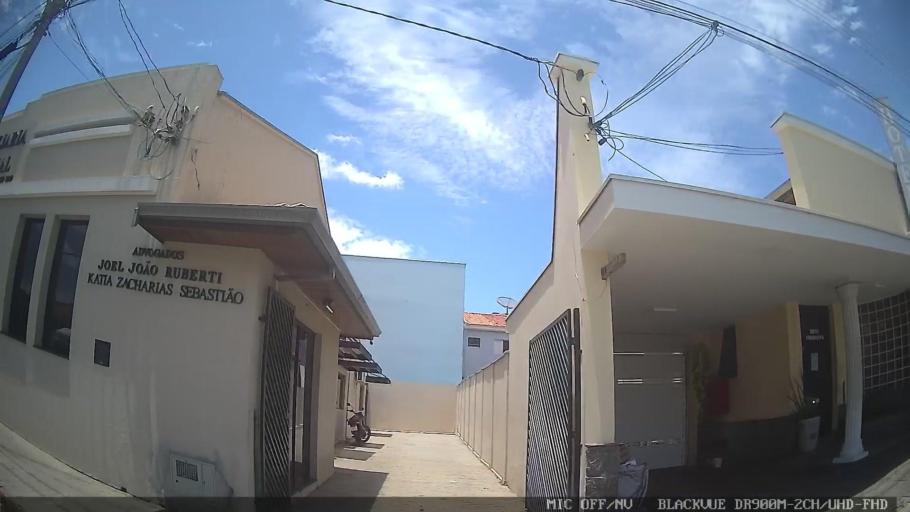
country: BR
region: Sao Paulo
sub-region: Laranjal Paulista
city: Laranjal Paulista
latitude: -23.0517
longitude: -47.8371
